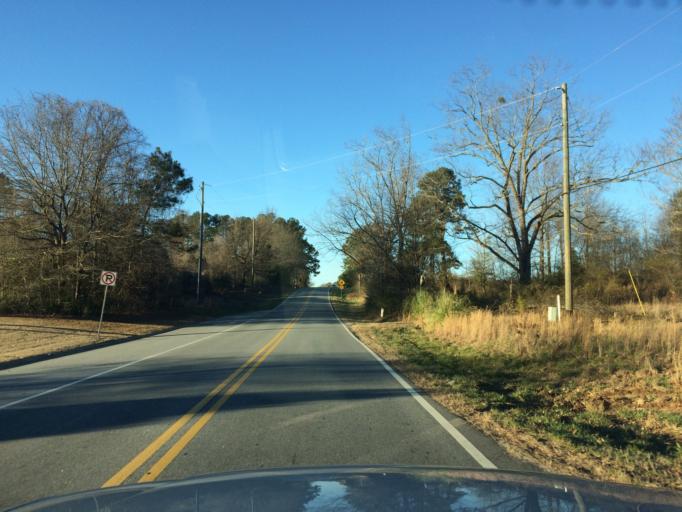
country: US
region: Georgia
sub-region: Barrow County
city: Winder
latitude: 33.9401
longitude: -83.7640
